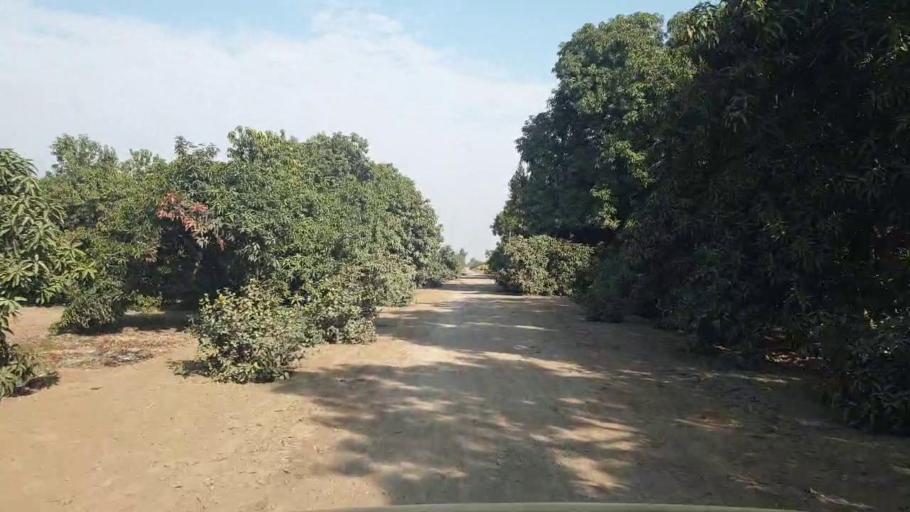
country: PK
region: Sindh
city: Tando Adam
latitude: 25.7555
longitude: 68.5882
